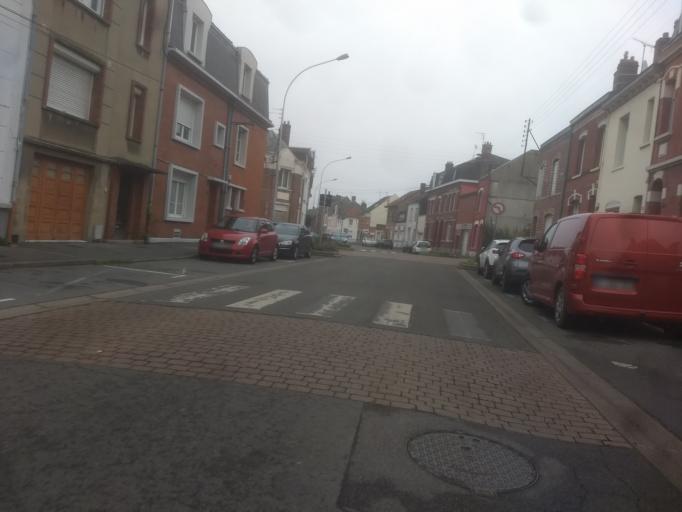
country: FR
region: Nord-Pas-de-Calais
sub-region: Departement du Pas-de-Calais
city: Arras
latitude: 50.2828
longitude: 2.7835
